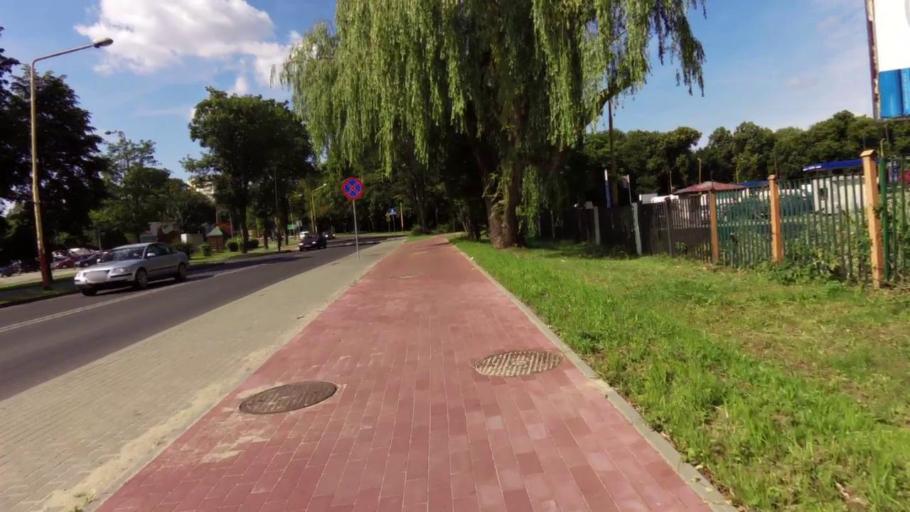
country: PL
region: West Pomeranian Voivodeship
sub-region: Powiat stargardzki
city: Stargard Szczecinski
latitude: 53.3431
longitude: 15.0519
